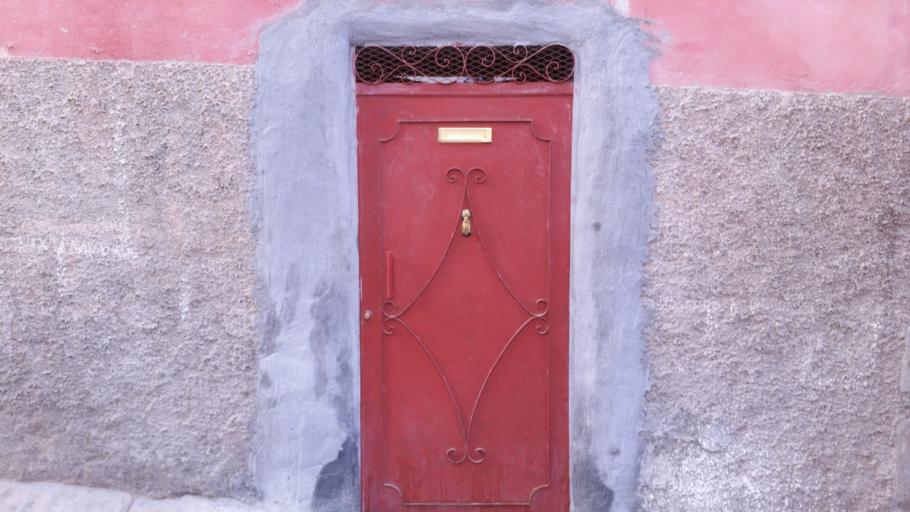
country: MA
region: Marrakech-Tensift-Al Haouz
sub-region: Marrakech
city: Marrakesh
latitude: 31.6185
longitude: -7.9823
